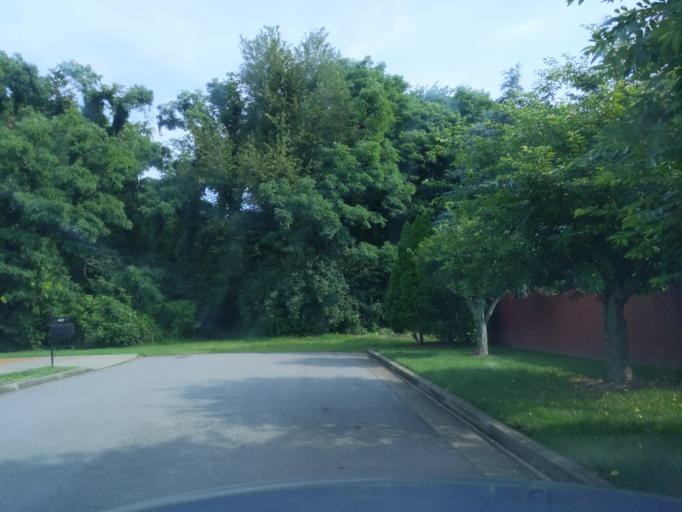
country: US
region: Tennessee
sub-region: Williamson County
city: Brentwood Estates
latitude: 36.0263
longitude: -86.7458
